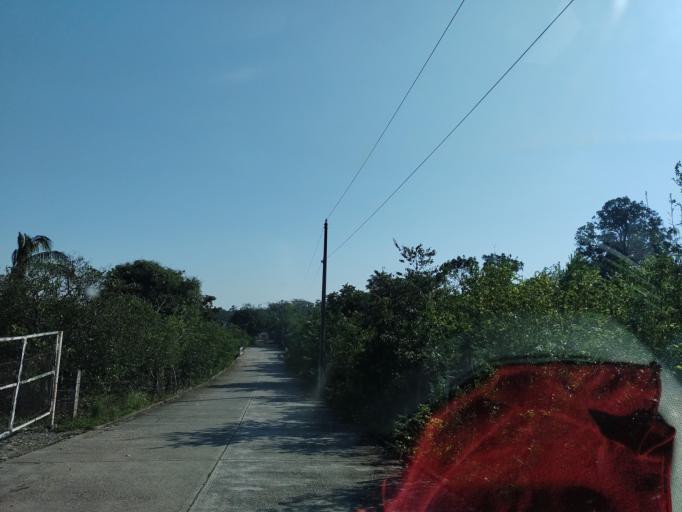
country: MX
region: Veracruz
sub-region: Papantla
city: Polutla
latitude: 20.4572
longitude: -97.2266
